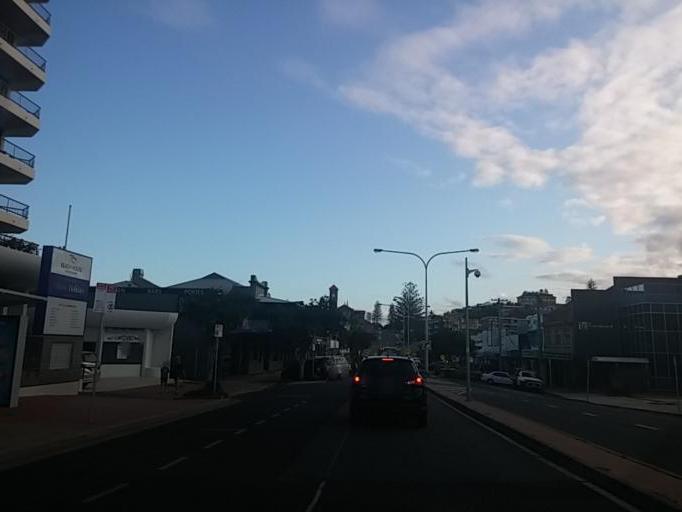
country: AU
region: New South Wales
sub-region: Tweed
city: Tweed Heads West
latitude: -28.1670
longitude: 153.5356
